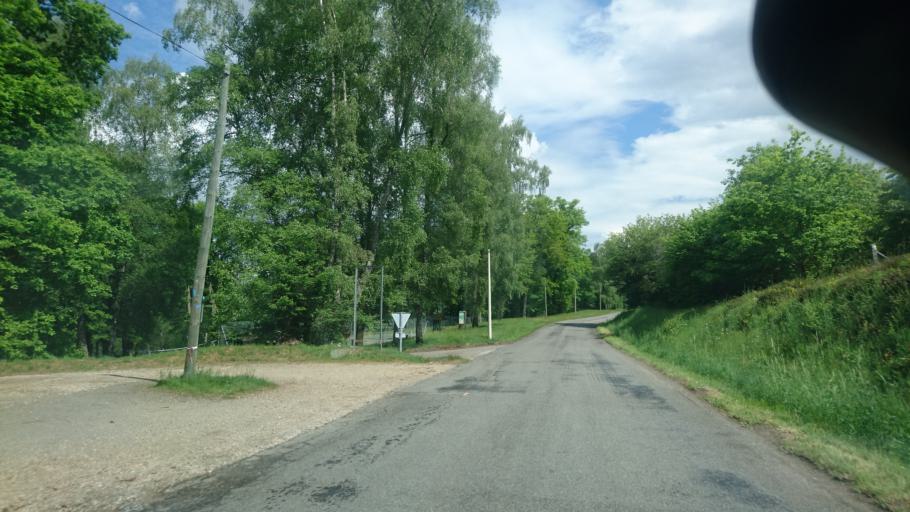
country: FR
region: Limousin
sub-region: Departement de la Haute-Vienne
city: Peyrat-le-Chateau
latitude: 45.7851
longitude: 1.8811
